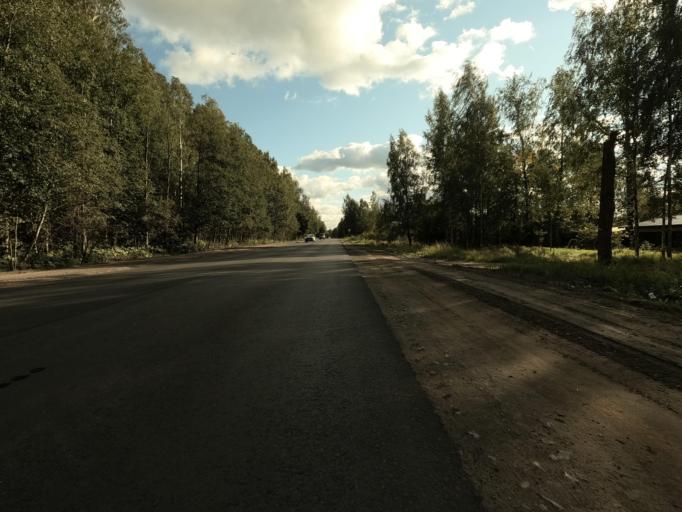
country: RU
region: Leningrad
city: Koltushi
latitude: 59.9295
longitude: 30.6642
